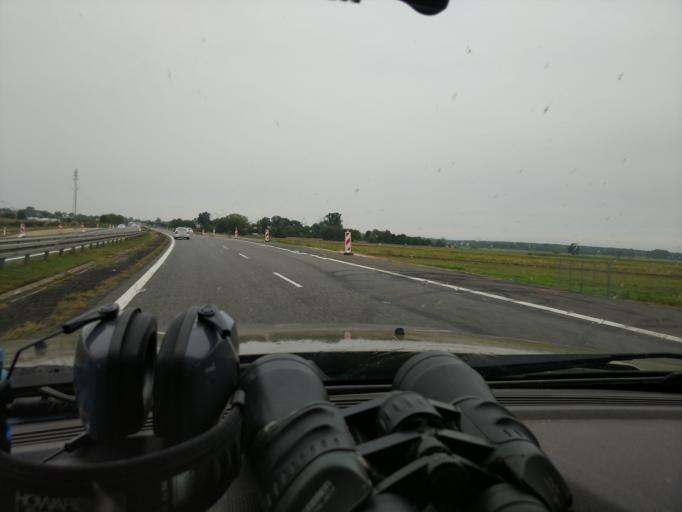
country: PL
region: Masovian Voivodeship
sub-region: Powiat wolominski
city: Radzymin
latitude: 52.4193
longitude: 21.2214
